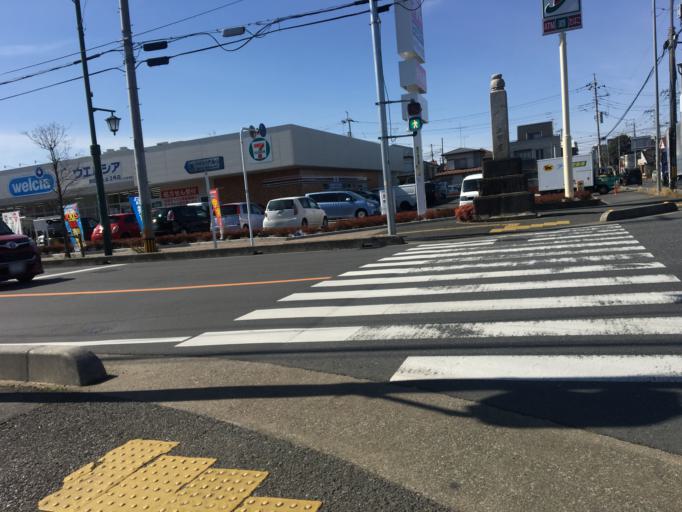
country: JP
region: Saitama
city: Asaka
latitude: 35.8010
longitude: 139.5694
